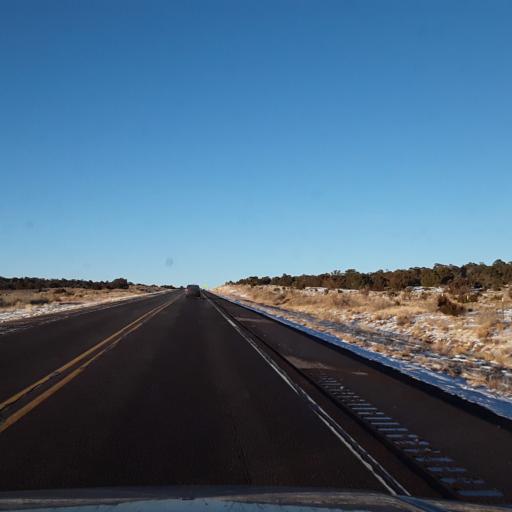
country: US
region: New Mexico
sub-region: Lincoln County
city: Carrizozo
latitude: 34.2138
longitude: -105.6478
